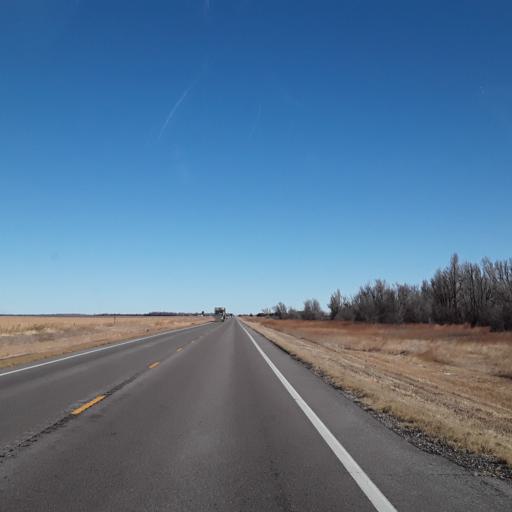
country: US
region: Kansas
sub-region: Pawnee County
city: Larned
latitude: 38.0965
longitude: -99.2132
